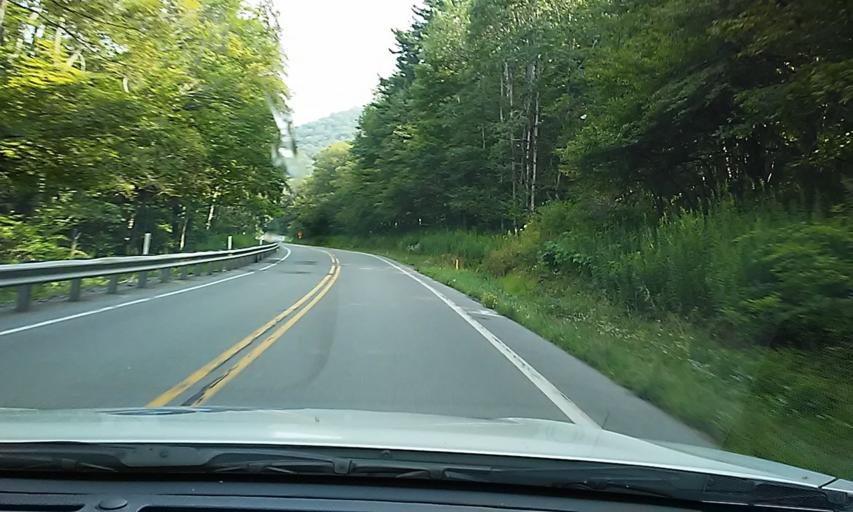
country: US
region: Pennsylvania
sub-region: Potter County
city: Galeton
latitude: 41.8174
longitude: -77.7931
